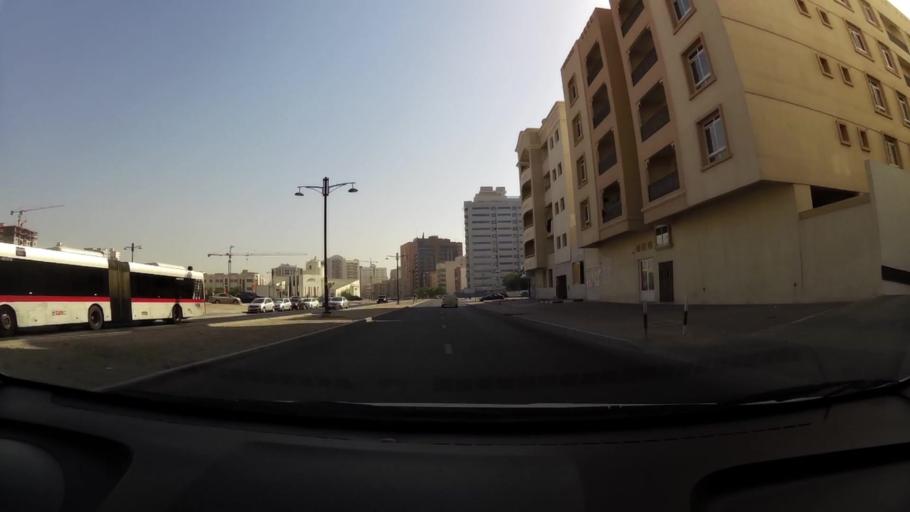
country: AE
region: Ash Shariqah
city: Sharjah
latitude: 25.2938
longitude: 55.3765
